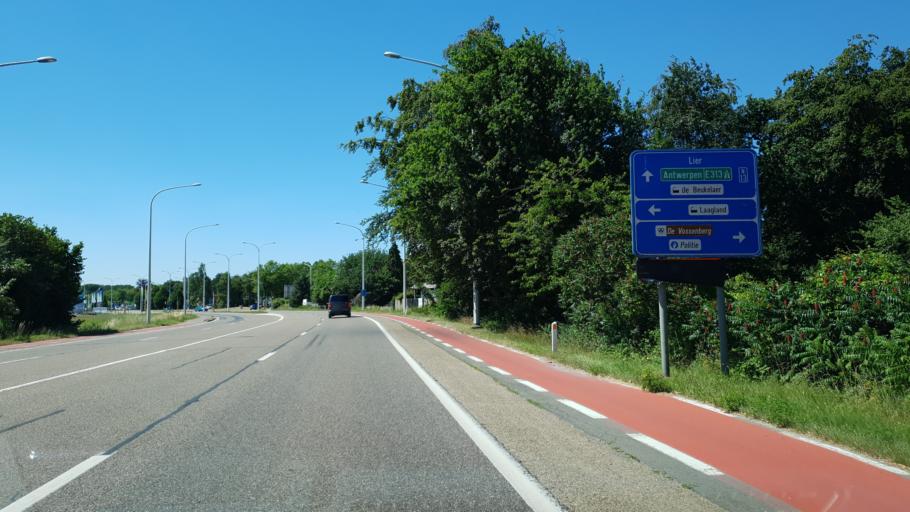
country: BE
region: Flanders
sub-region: Provincie Antwerpen
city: Herentals
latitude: 51.1736
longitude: 4.8219
